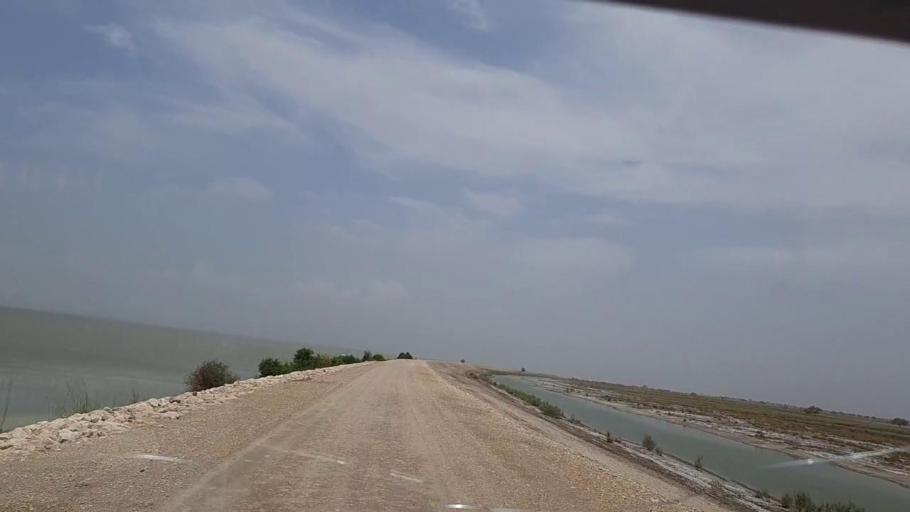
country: PK
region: Sindh
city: Sehwan
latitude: 26.4208
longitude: 67.7266
